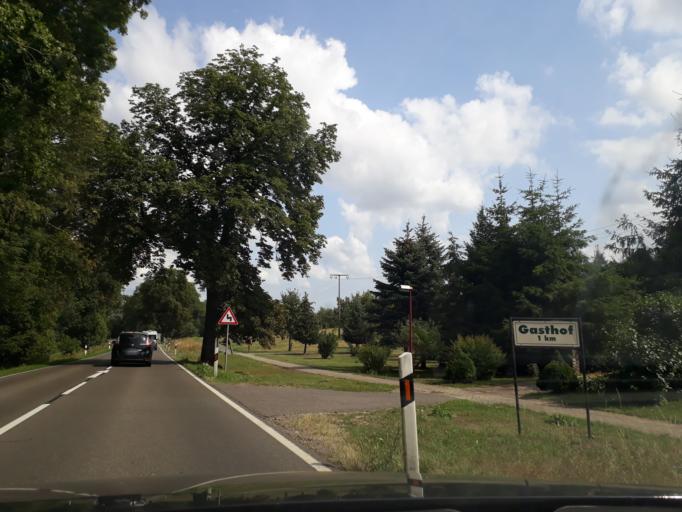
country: DE
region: Mecklenburg-Vorpommern
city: Lassan
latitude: 53.9037
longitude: 13.7714
